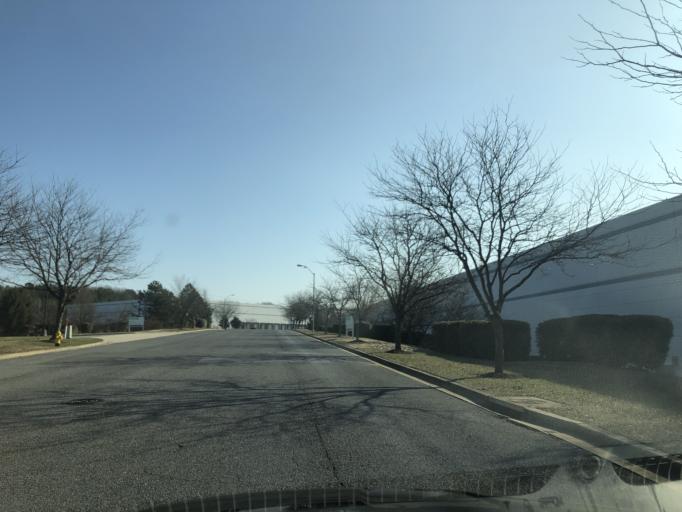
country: US
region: Maryland
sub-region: Anne Arundel County
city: Odenton
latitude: 39.0885
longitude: -76.6899
